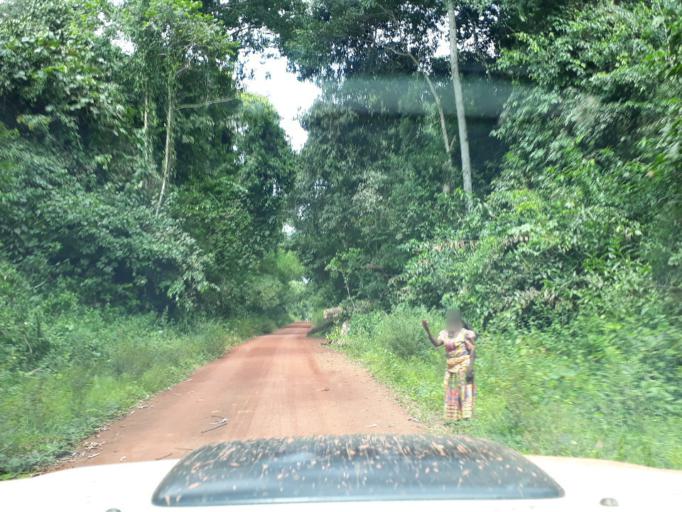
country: CD
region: Eastern Province
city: Buta
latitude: 2.3148
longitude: 25.0016
